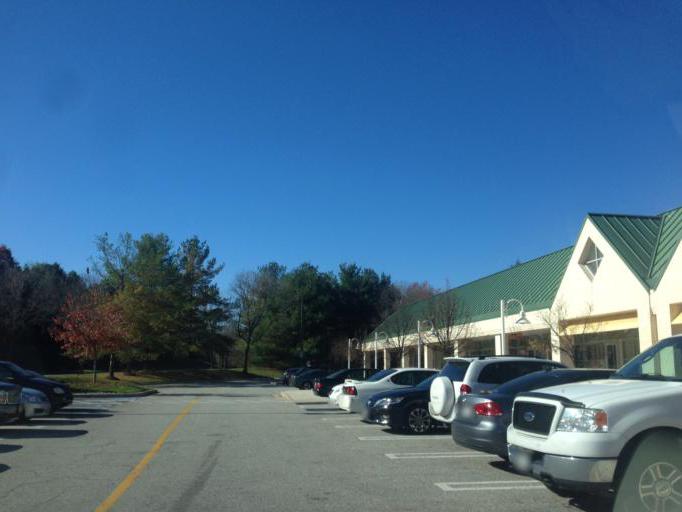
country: US
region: Maryland
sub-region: Howard County
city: Riverside
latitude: 39.1943
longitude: -76.8830
